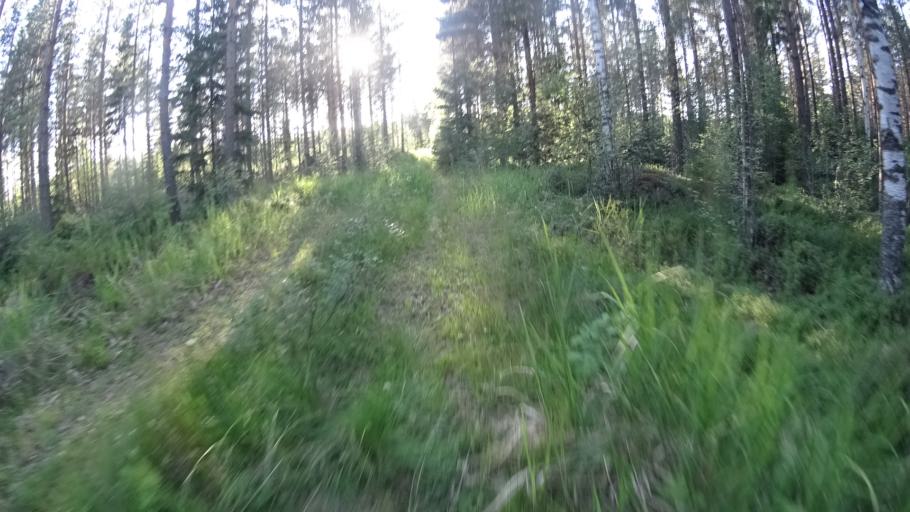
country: FI
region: Uusimaa
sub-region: Helsinki
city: Karkkila
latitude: 60.5920
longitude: 24.0964
